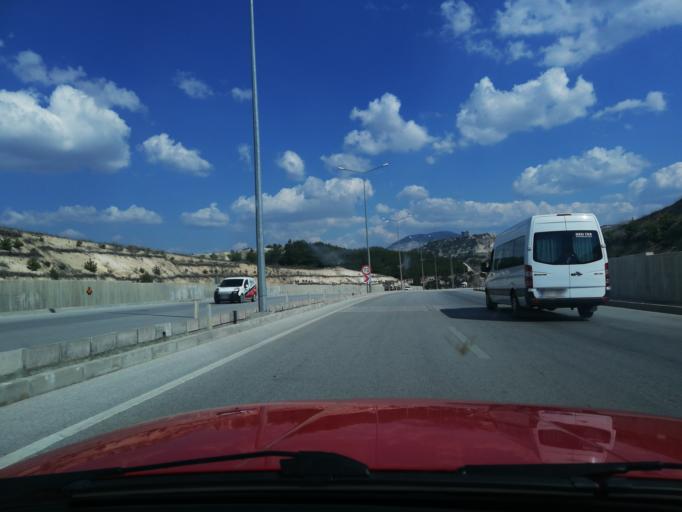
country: TR
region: Burdur
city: Burdur
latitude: 37.7010
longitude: 30.3164
